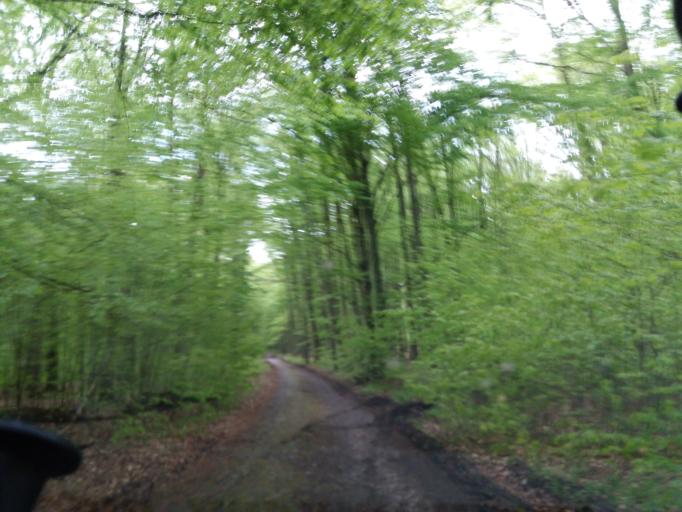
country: PL
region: West Pomeranian Voivodeship
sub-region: Powiat choszczenski
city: Drawno
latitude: 53.0985
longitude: 15.8921
